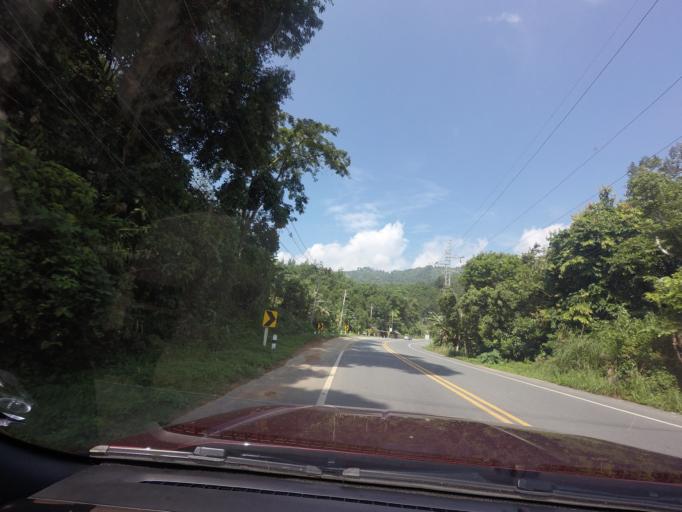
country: TH
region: Yala
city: Betong
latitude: 5.9174
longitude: 101.1727
